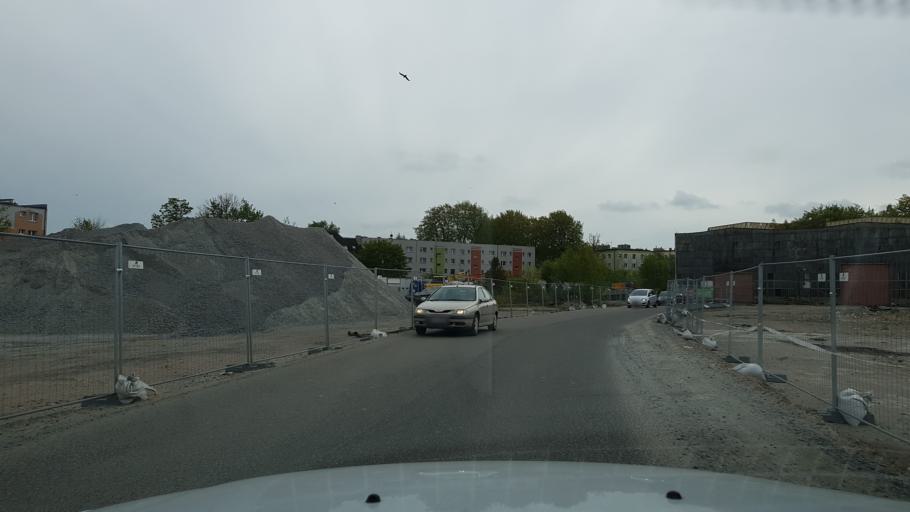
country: PL
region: Pomeranian Voivodeship
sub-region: Powiat slupski
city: Ustka
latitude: 54.5793
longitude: 16.8537
